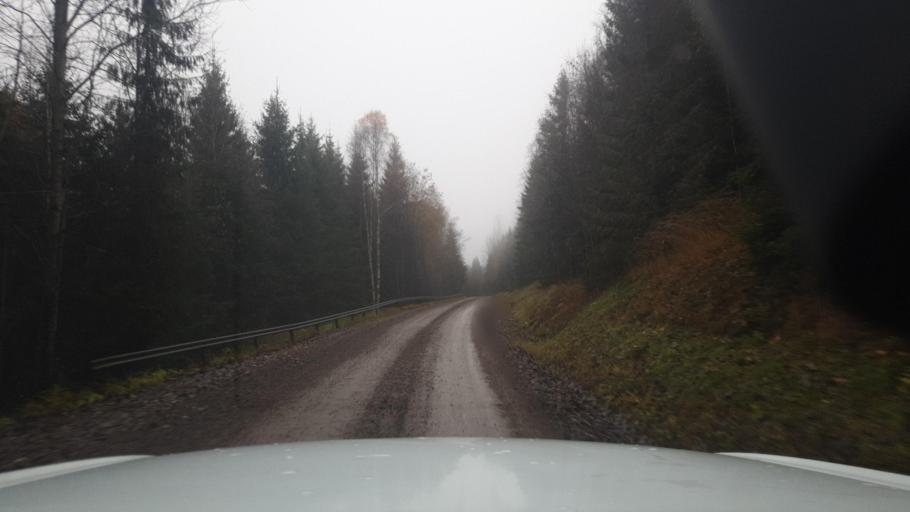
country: SE
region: Vaermland
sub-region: Arvika Kommun
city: Arvika
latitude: 60.0105
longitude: 12.6519
